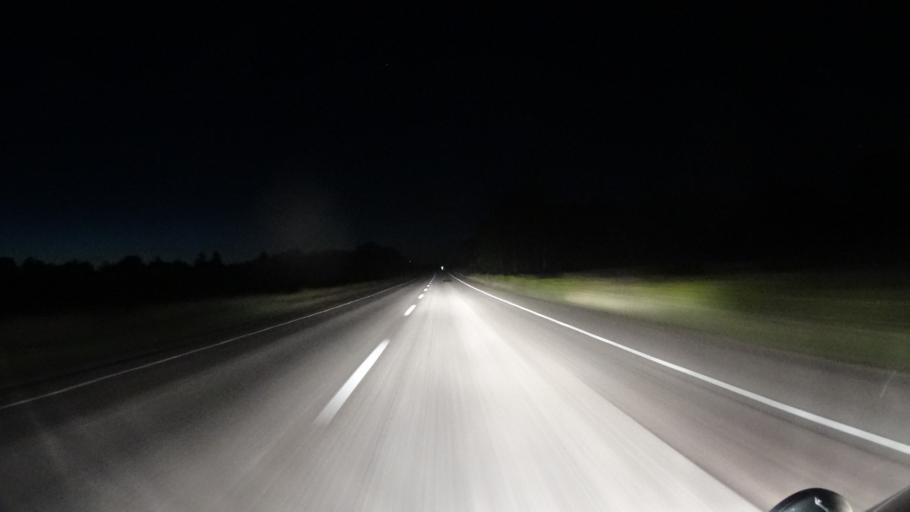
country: SE
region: OEstergoetland
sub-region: Odeshogs Kommun
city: OEdeshoeg
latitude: 58.2538
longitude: 14.7313
